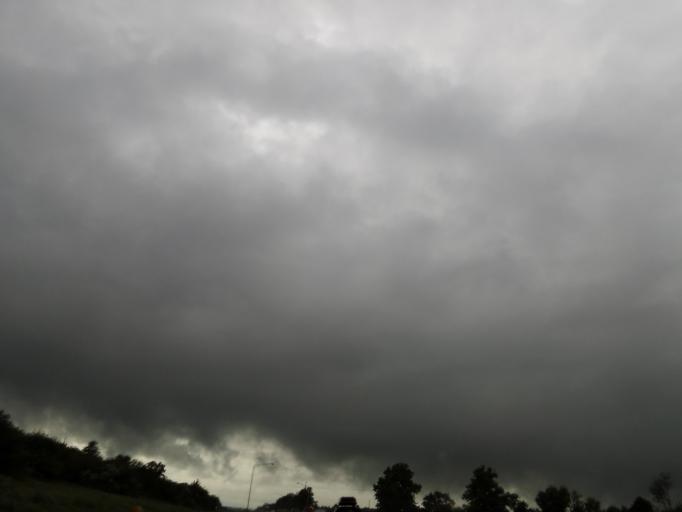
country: US
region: Illinois
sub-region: Jefferson County
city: Mount Vernon
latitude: 38.3371
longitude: -88.9570
